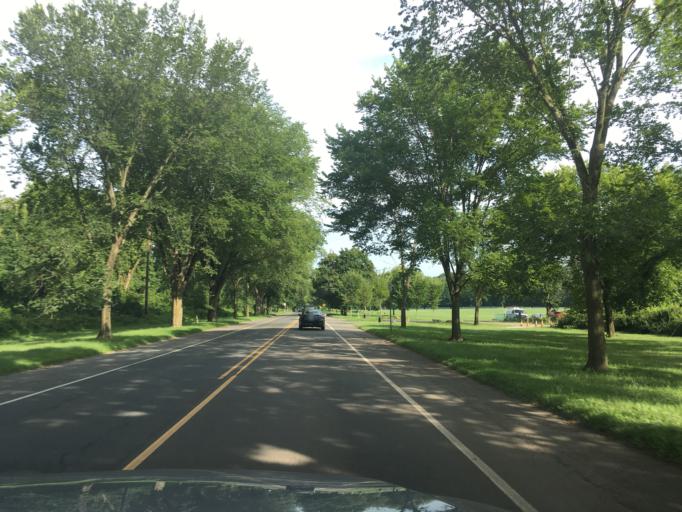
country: US
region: New Jersey
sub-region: Mercer County
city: Princeton
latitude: 40.3357
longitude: -74.6434
